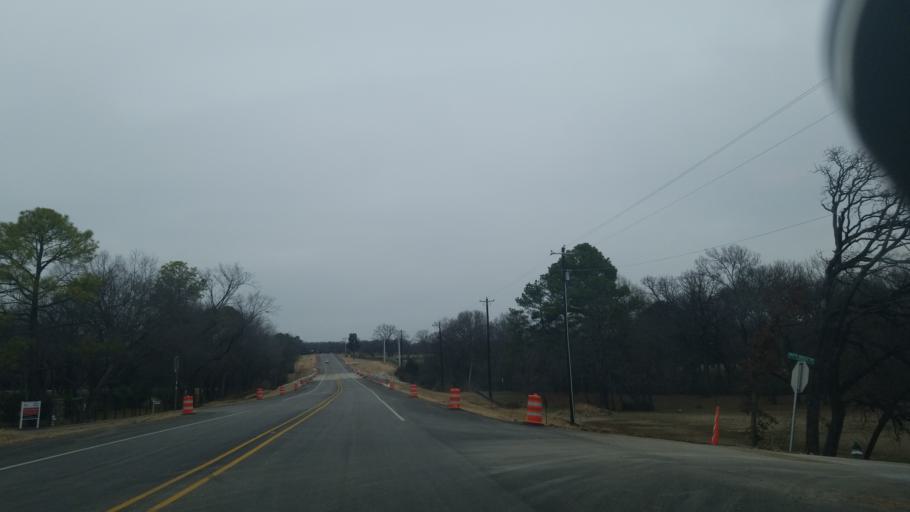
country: US
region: Texas
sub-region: Denton County
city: Argyle
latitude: 33.1230
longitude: -97.1396
